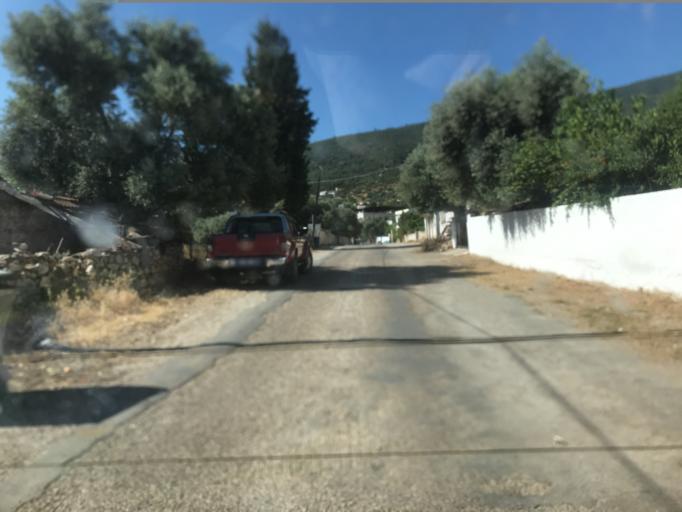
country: TR
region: Mugla
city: Kiulukioi
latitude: 37.3669
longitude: 27.4945
